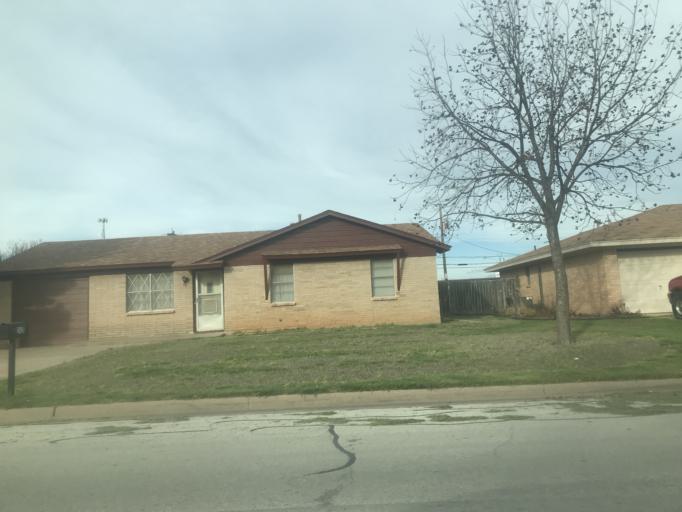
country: US
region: Texas
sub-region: Taylor County
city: Abilene
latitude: 32.3967
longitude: -99.7540
